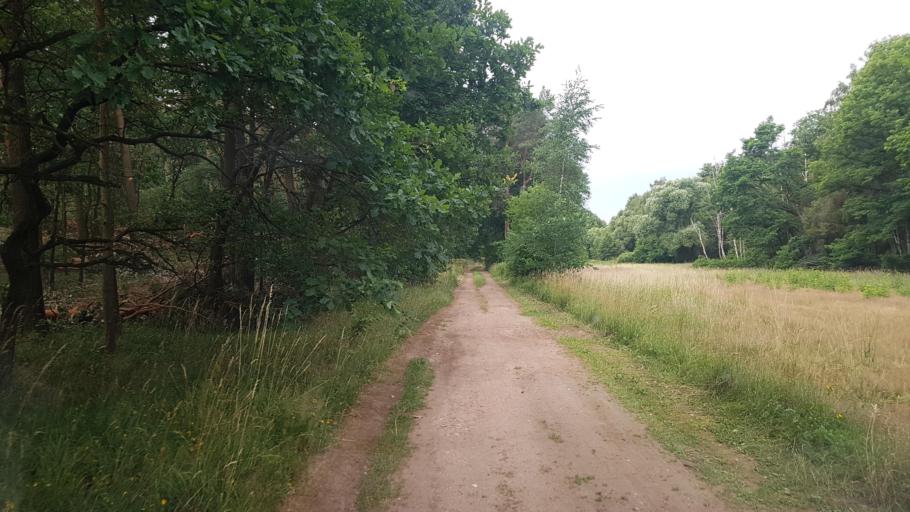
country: DE
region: Saxony-Anhalt
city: Abtsdorf
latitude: 51.8888
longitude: 12.7159
